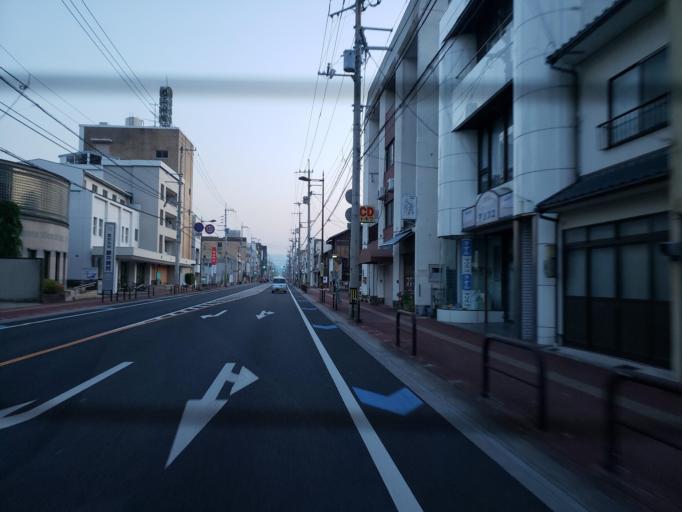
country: JP
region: Ehime
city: Hojo
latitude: 34.0607
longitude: 132.9940
